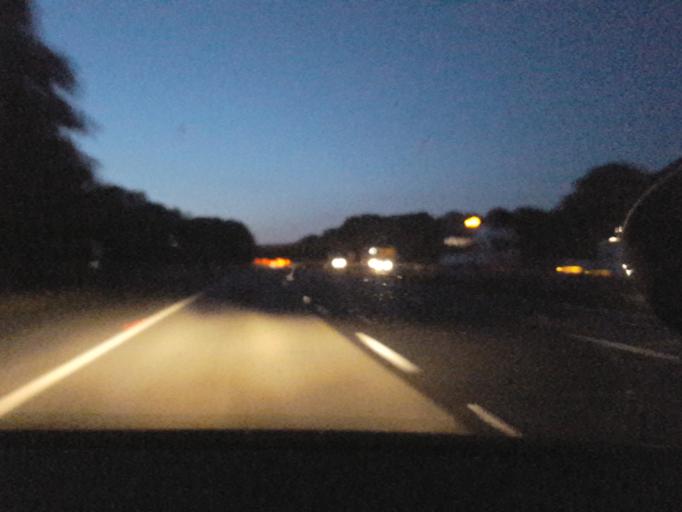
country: GB
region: England
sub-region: Leicestershire
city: Markfield
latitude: 52.6838
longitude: -1.2894
